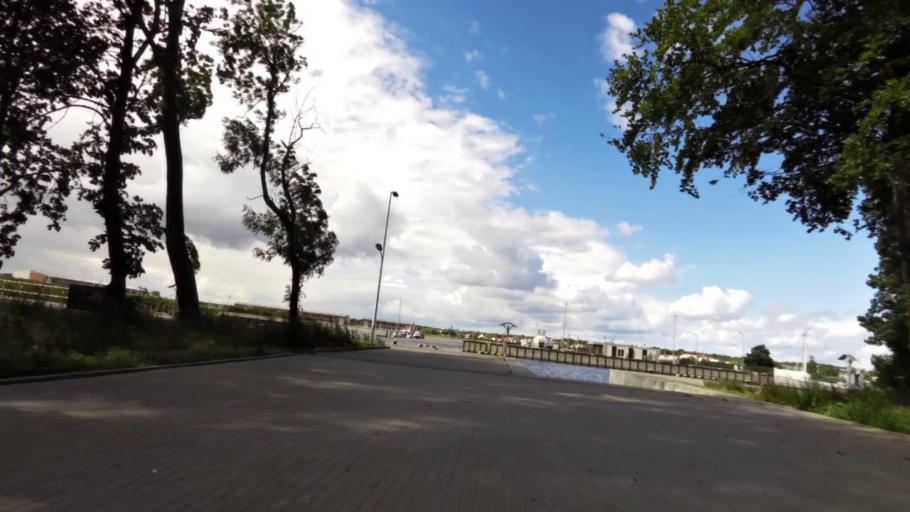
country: PL
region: West Pomeranian Voivodeship
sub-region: Powiat slawienski
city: Darlowo
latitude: 54.4349
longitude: 16.3894
